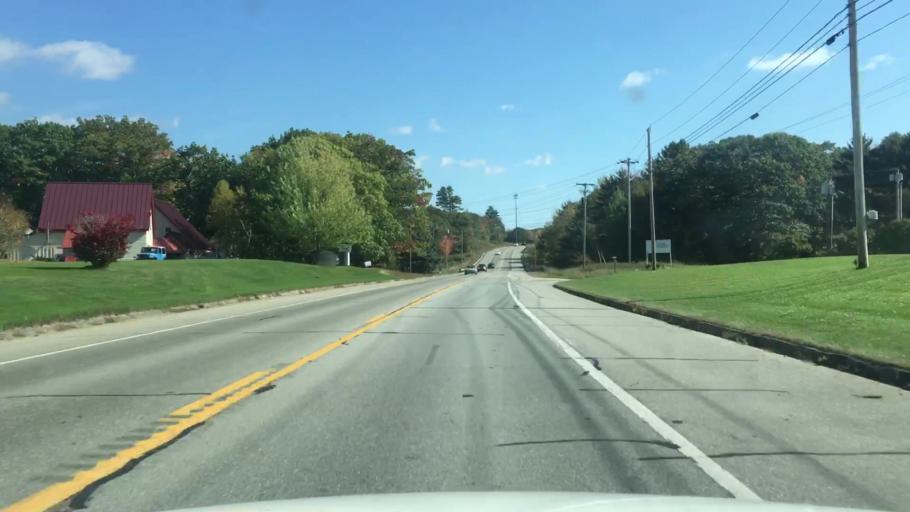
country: US
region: Maine
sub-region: Knox County
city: Warren
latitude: 44.1208
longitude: -69.2835
